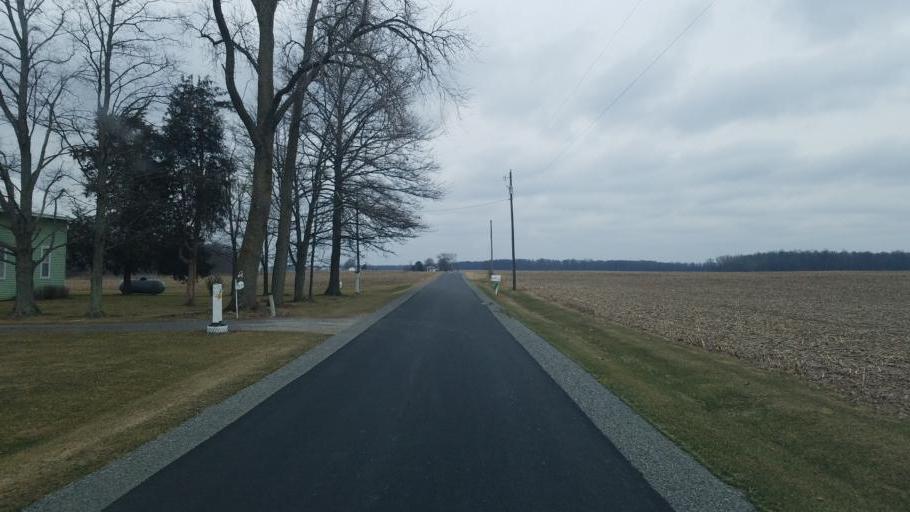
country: US
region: Ohio
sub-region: Morrow County
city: Mount Gilead
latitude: 40.5906
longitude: -82.8950
